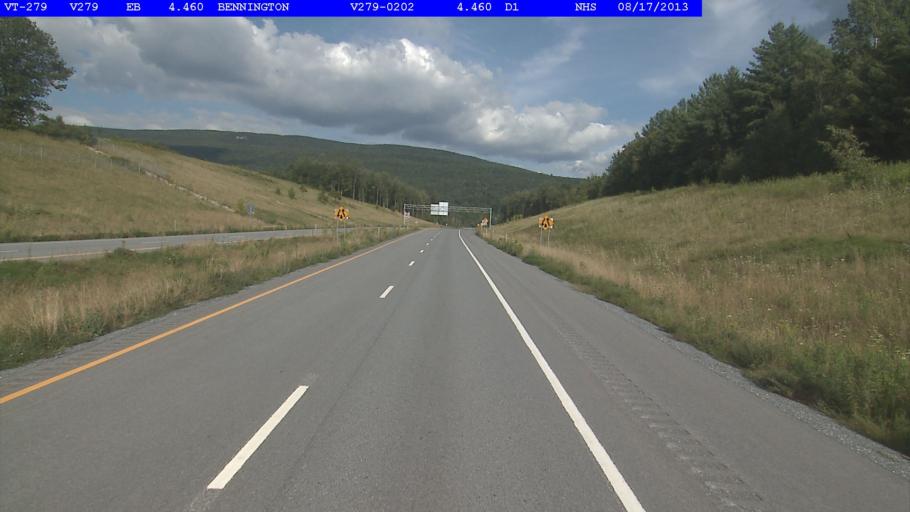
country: US
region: Vermont
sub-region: Bennington County
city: Bennington
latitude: 42.9016
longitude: -73.1905
